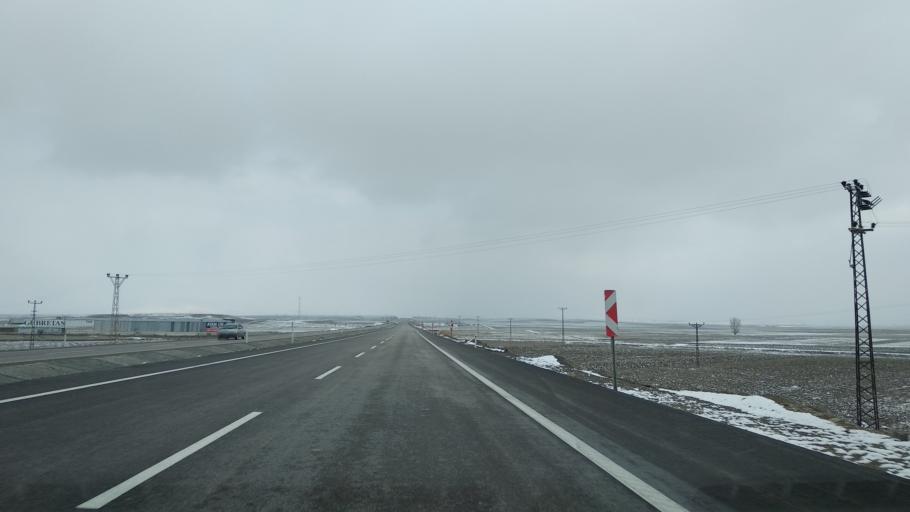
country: TR
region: Kayseri
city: Elbasi
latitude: 38.6541
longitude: 36.0130
